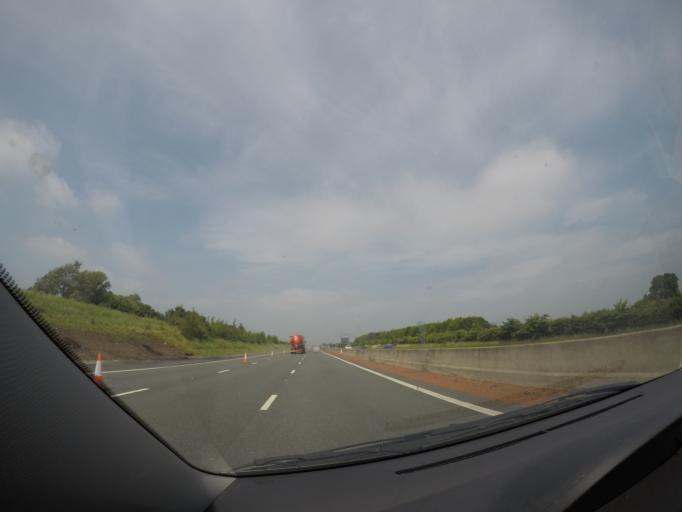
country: GB
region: England
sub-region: North Yorkshire
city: Bedale
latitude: 54.2529
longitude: -1.5094
